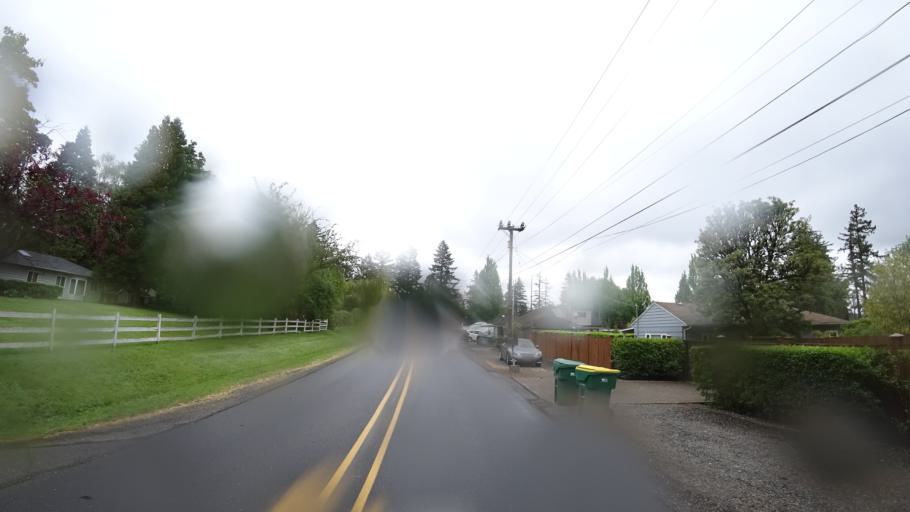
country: US
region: Oregon
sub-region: Washington County
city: Raleigh Hills
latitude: 45.4794
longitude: -122.7643
